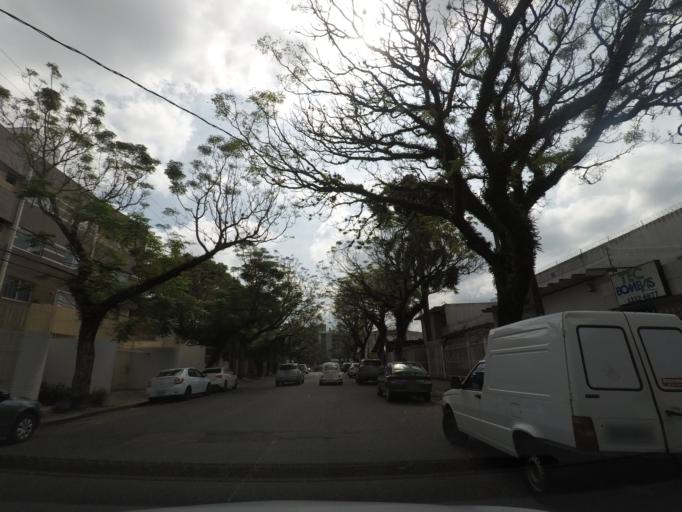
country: BR
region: Parana
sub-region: Curitiba
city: Curitiba
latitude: -25.4498
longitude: -49.2555
